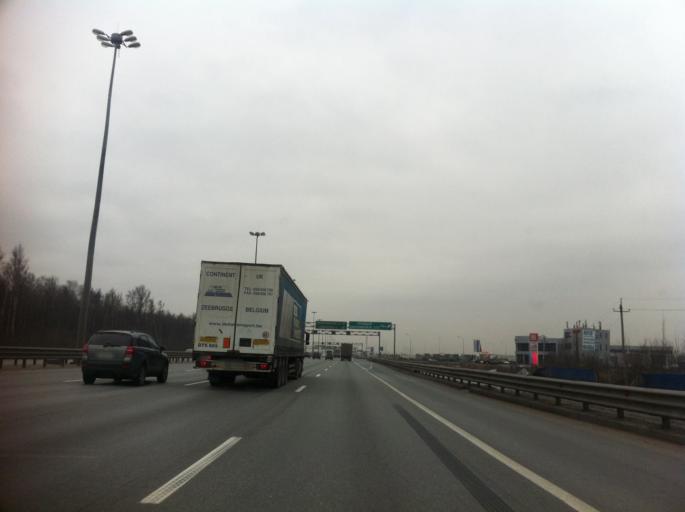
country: RU
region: Leningrad
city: Rybatskoye
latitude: 59.8826
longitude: 30.5267
